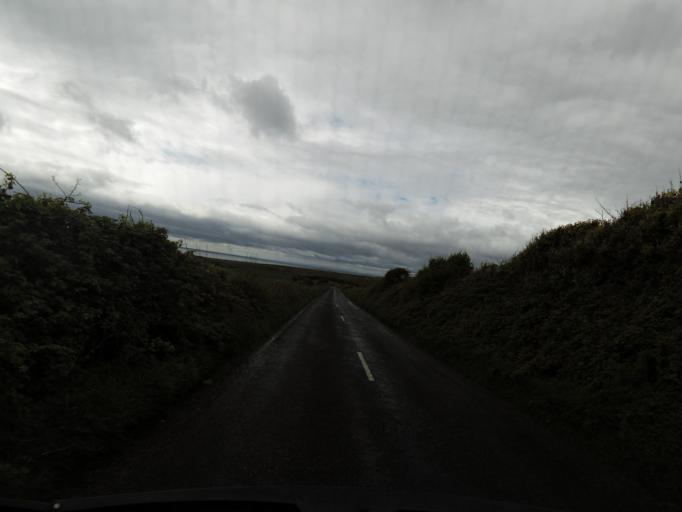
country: IE
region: Connaught
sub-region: County Galway
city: Bearna
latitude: 53.0526
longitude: -9.3473
